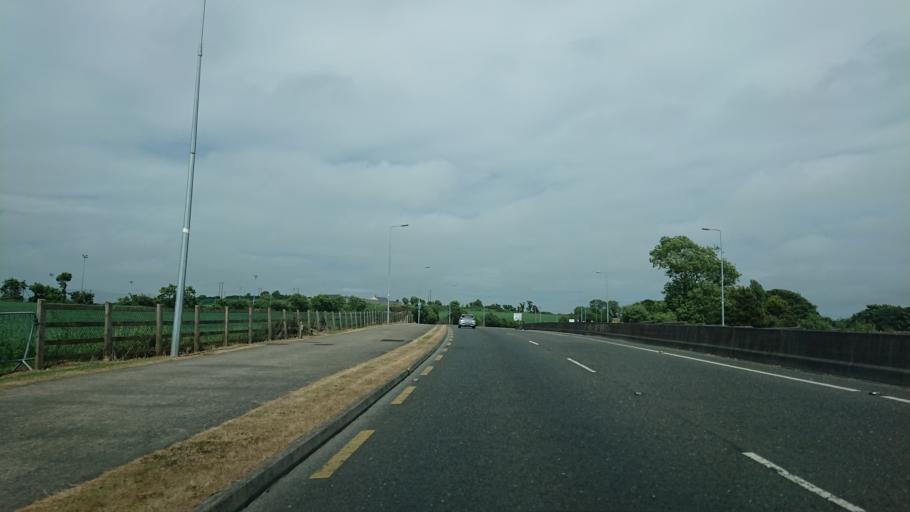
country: IE
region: Munster
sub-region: Waterford
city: Waterford
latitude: 52.2350
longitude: -7.1013
